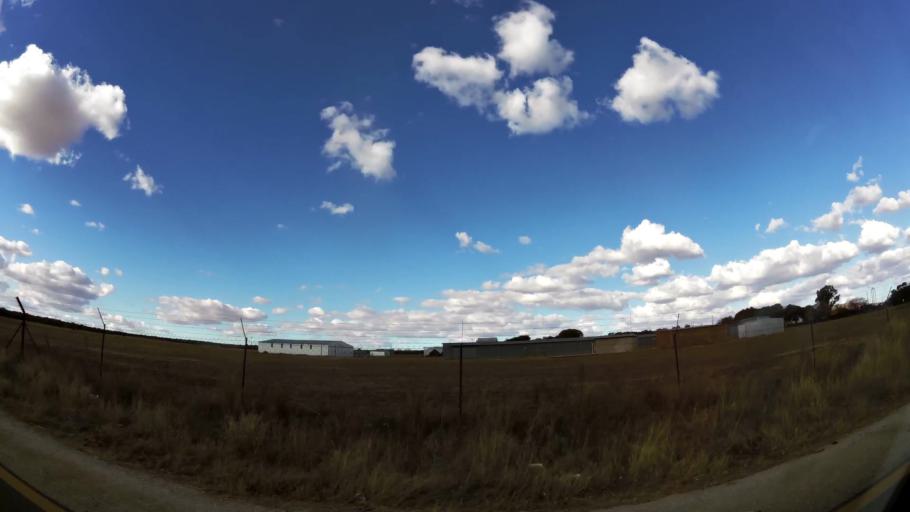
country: ZA
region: Limpopo
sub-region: Capricorn District Municipality
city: Polokwane
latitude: -23.9328
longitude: 29.4723
